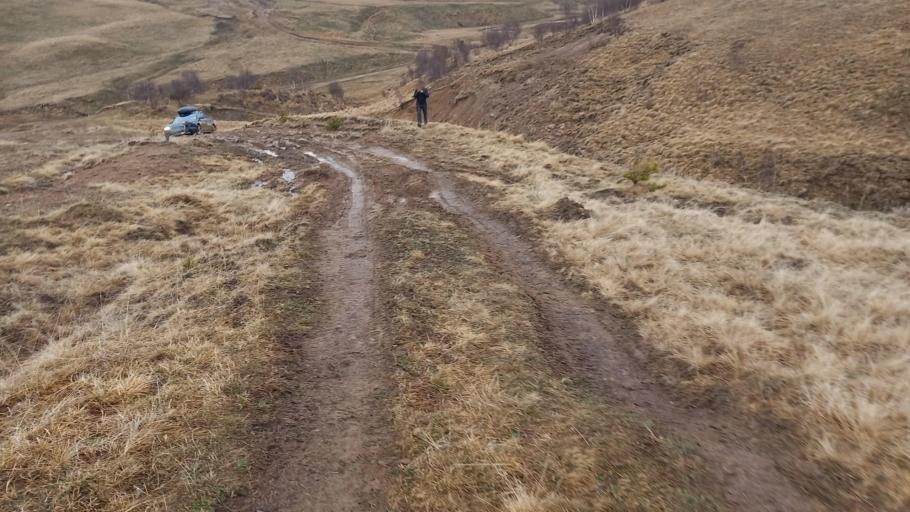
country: RU
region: Kabardino-Balkariya
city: Terskol
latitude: 43.5224
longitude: 42.4269
